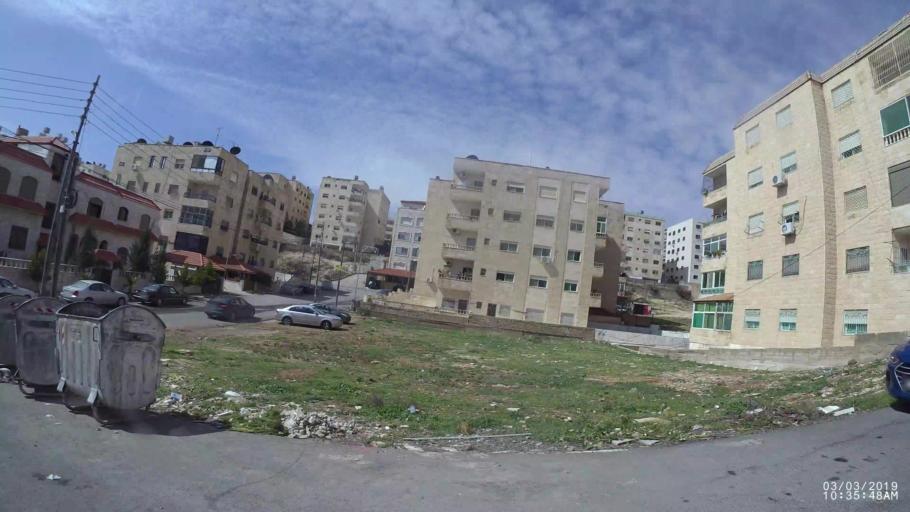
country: JO
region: Amman
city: Al Jubayhah
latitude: 31.9958
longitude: 35.9072
